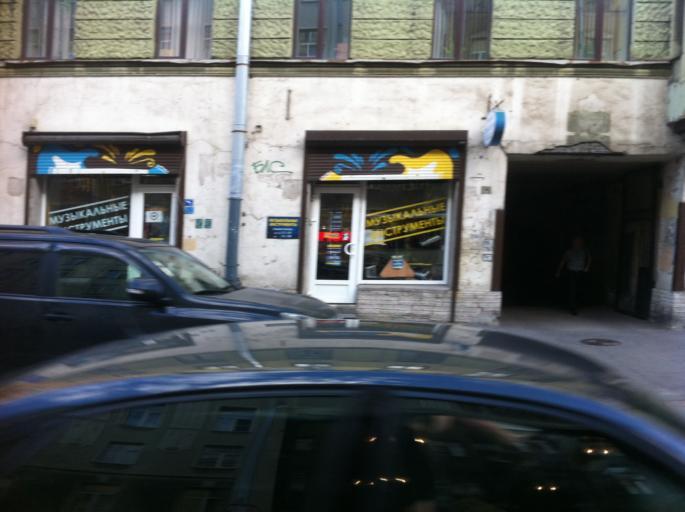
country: RU
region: St.-Petersburg
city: Admiralteisky
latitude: 59.9039
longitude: 30.2741
